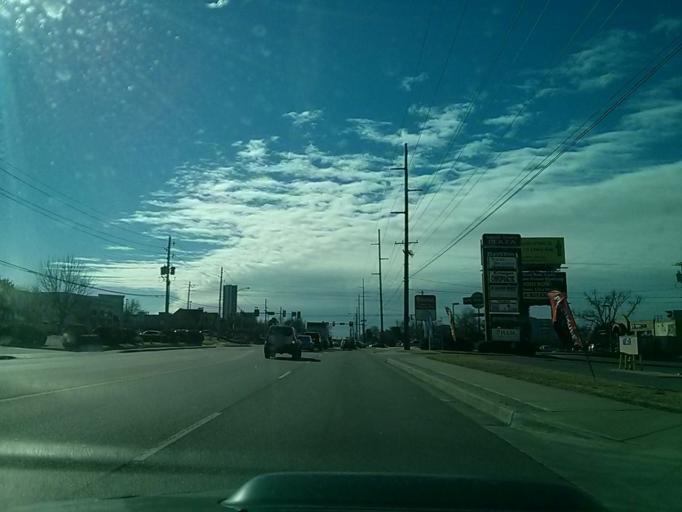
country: US
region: Oklahoma
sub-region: Tulsa County
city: Jenks
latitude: 36.0623
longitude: -95.9580
